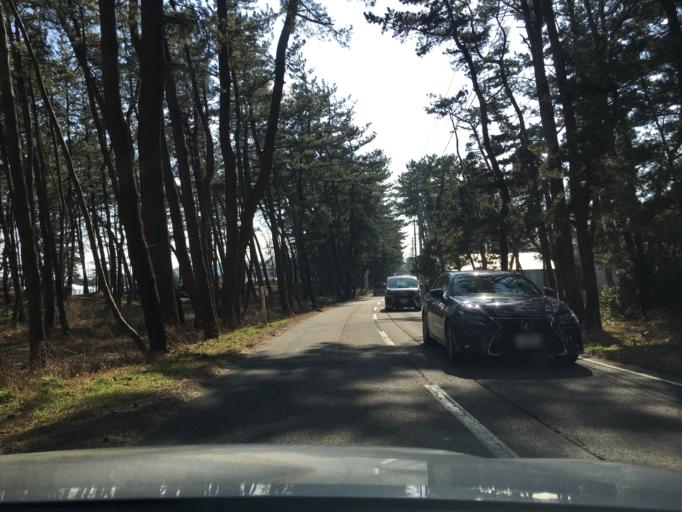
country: JP
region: Yamagata
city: Tsuruoka
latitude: 38.8070
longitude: 139.7774
